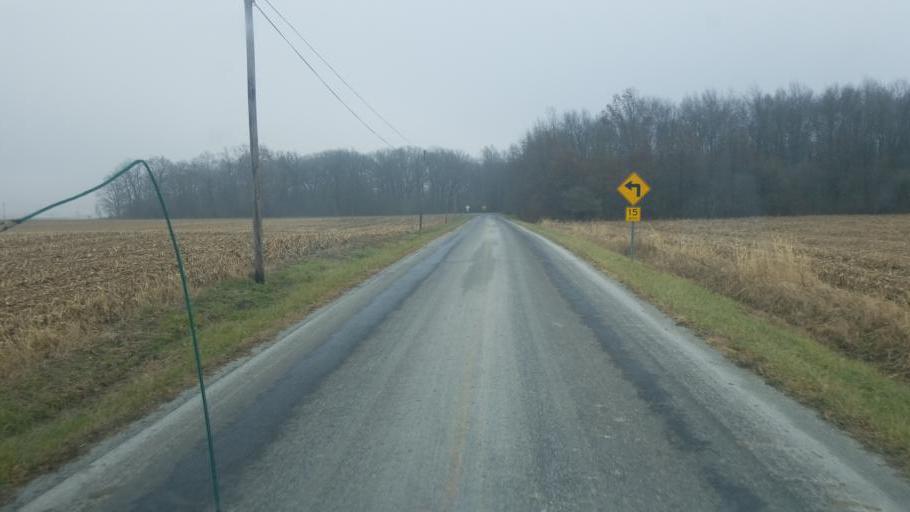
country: US
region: Ohio
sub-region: Hardin County
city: Kenton
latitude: 40.5649
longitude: -83.4703
